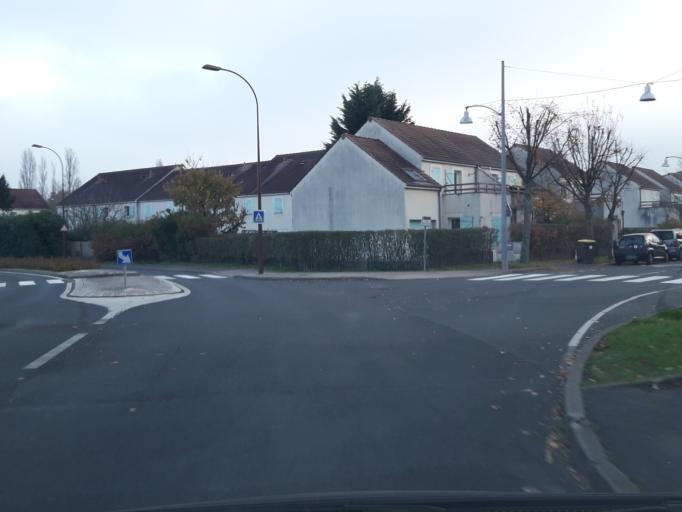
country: FR
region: Ile-de-France
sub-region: Departement de l'Essonne
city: Fleury-Merogis
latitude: 48.6412
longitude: 2.3492
